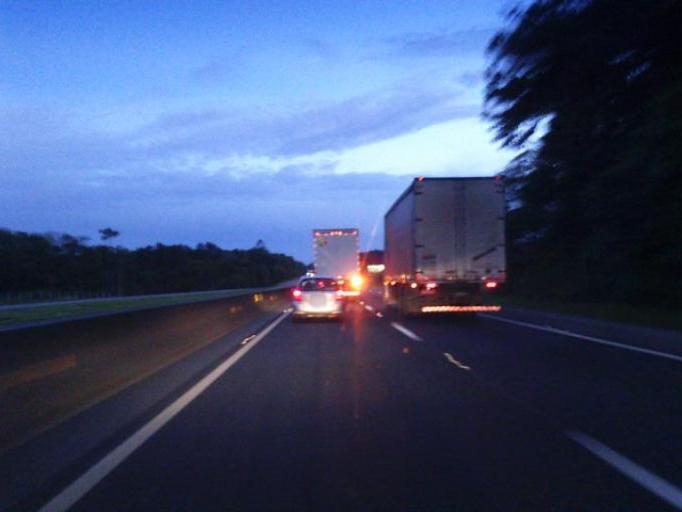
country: BR
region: Santa Catarina
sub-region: Barra Velha
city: Barra Velha
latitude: -26.4994
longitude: -48.7302
